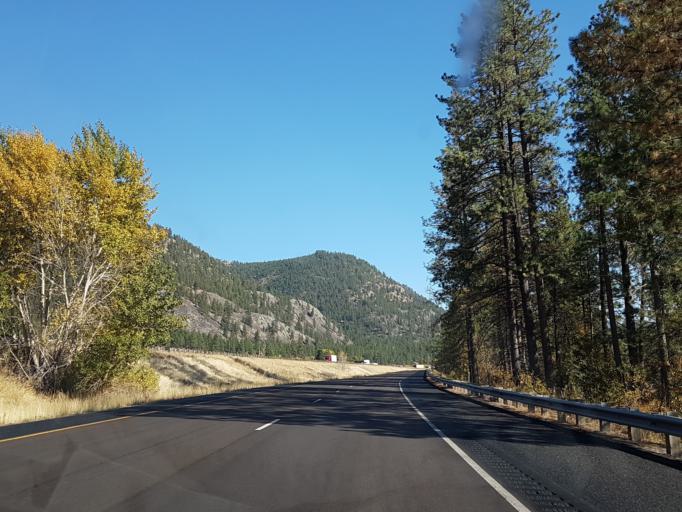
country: US
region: Montana
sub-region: Missoula County
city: Frenchtown
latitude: 47.0203
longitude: -114.5214
